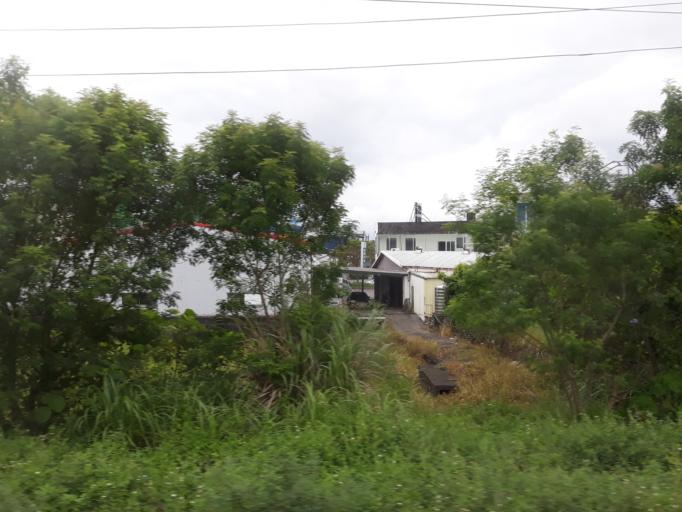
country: TW
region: Taiwan
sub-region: Yilan
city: Yilan
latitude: 24.7097
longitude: 121.7735
